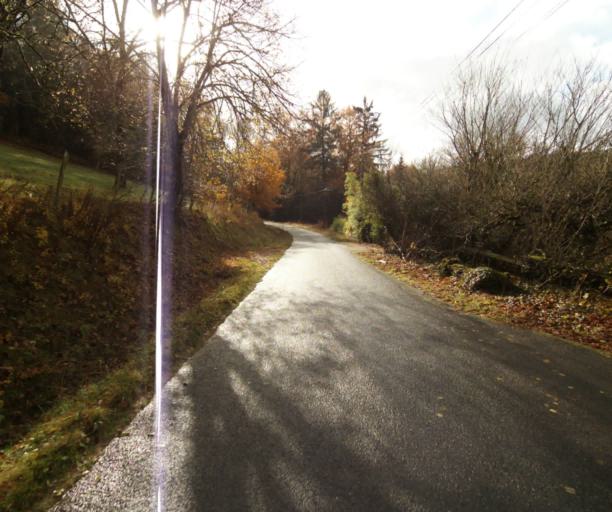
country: FR
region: Limousin
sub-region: Departement de la Correze
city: Cornil
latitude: 45.2086
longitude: 1.6587
